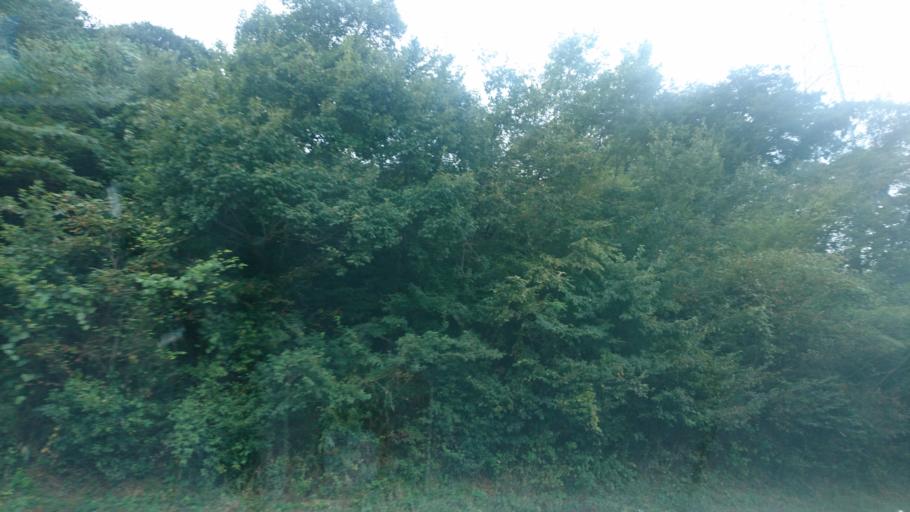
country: JP
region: Fukushima
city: Sukagawa
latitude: 37.3096
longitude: 140.2669
